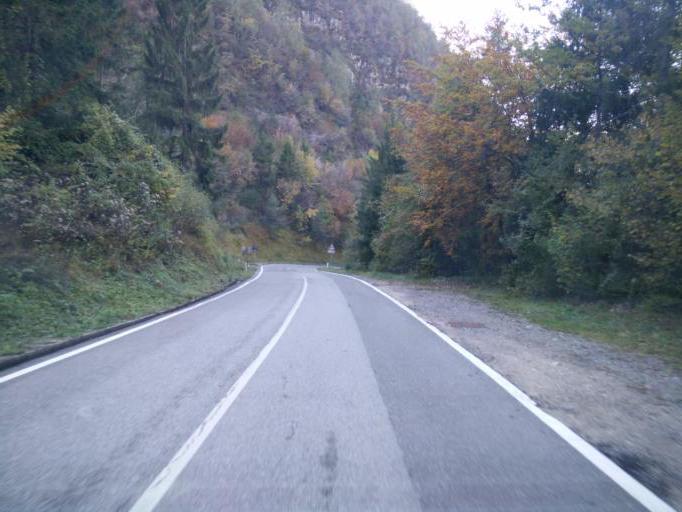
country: IT
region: Lombardy
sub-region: Provincia di Brescia
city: Capovalle
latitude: 45.7468
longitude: 10.5326
